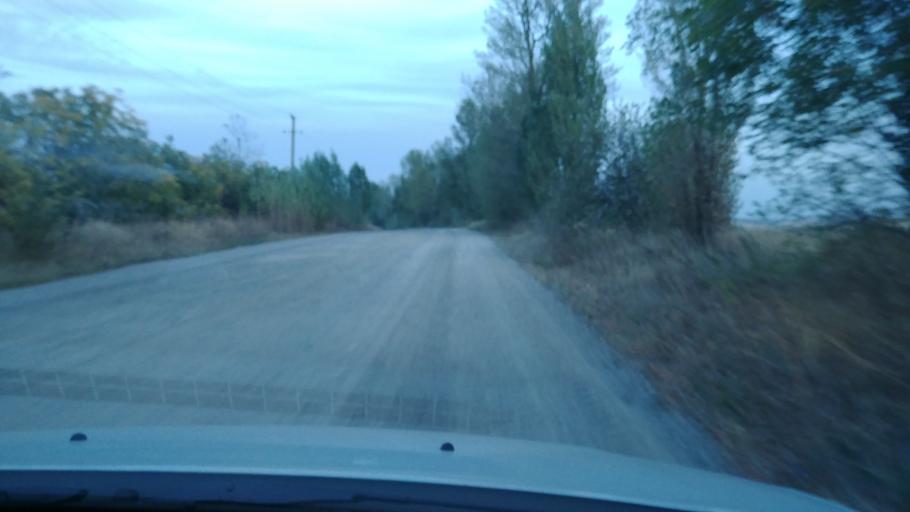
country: MD
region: Rezina
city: Saharna
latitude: 47.6801
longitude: 28.9179
